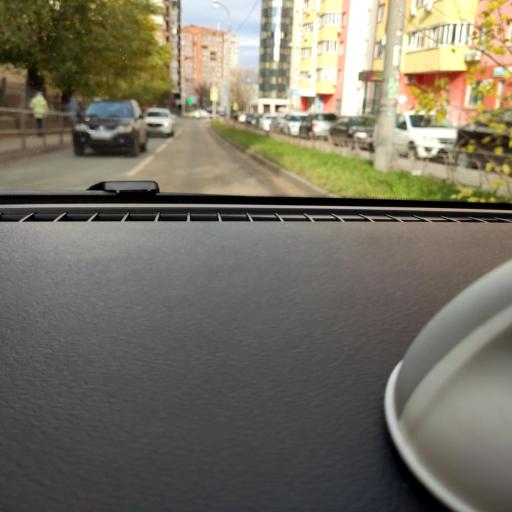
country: RU
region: Samara
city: Samara
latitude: 53.2169
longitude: 50.1661
